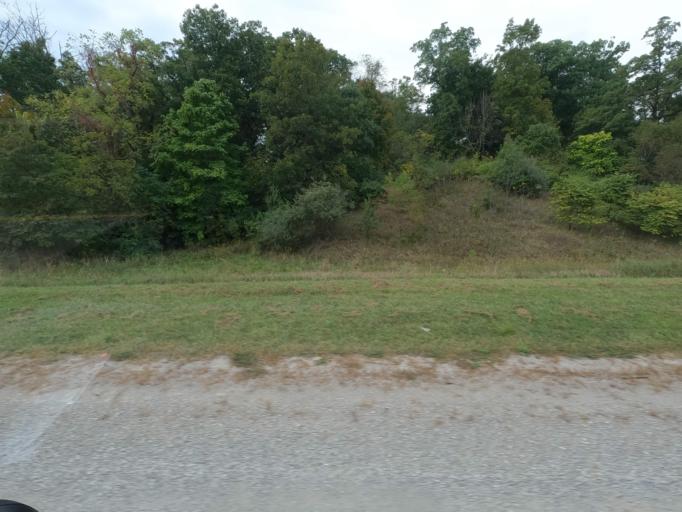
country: US
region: Iowa
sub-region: Wapello County
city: Ottumwa
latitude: 41.0332
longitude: -92.3766
